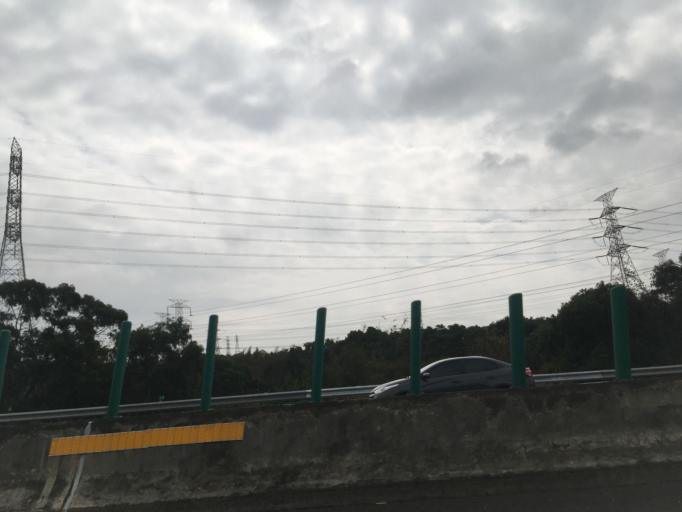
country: TW
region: Taiwan
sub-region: Changhua
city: Chang-hua
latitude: 24.1913
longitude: 120.5635
